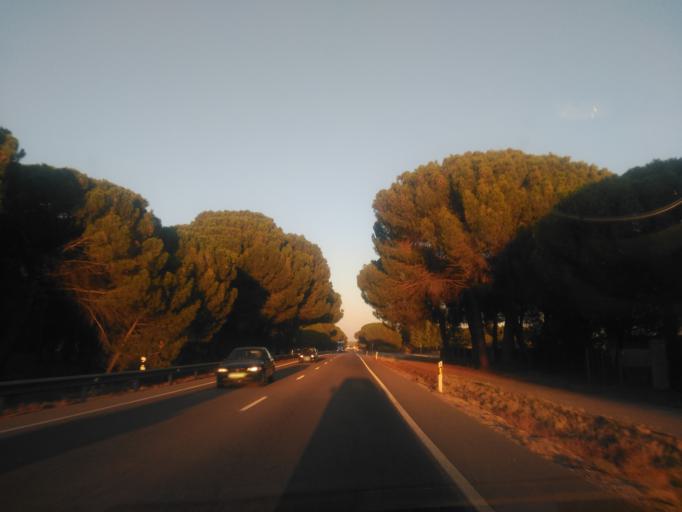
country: ES
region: Castille and Leon
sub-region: Provincia de Valladolid
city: Traspinedo
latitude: 41.5983
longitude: -4.5009
